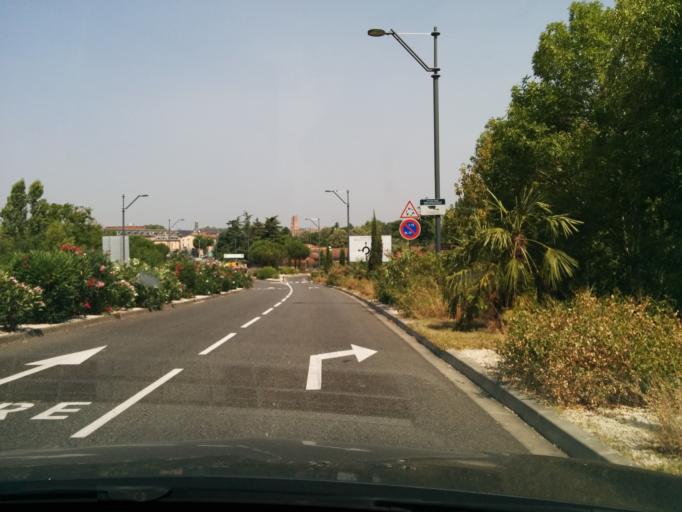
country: FR
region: Midi-Pyrenees
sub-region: Departement du Tarn
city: Albi
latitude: 43.9166
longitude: 2.1533
